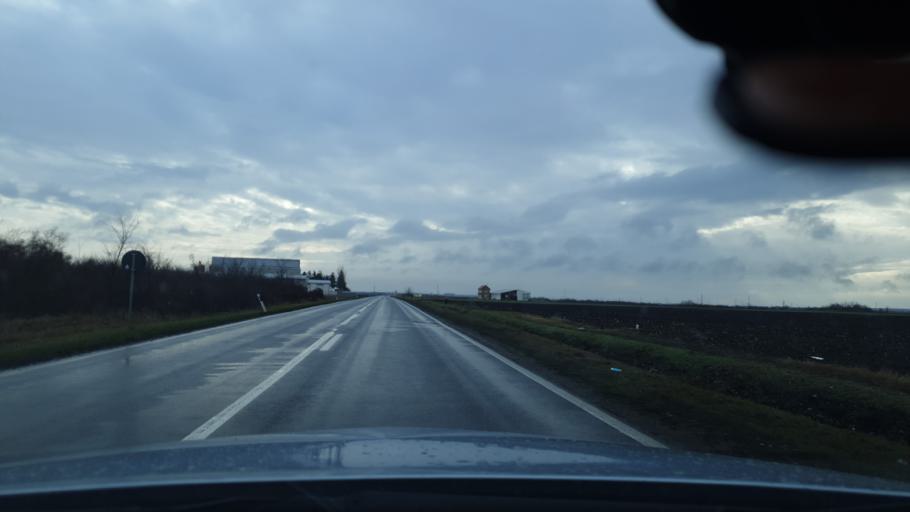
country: RS
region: Autonomna Pokrajina Vojvodina
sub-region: Juznobanatski Okrug
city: Kovin
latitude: 44.8076
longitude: 20.8927
